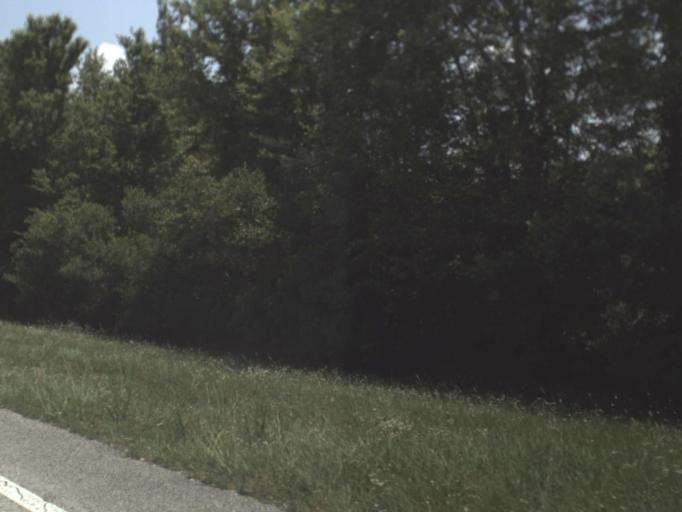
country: US
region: Florida
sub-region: Duval County
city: Baldwin
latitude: 30.2135
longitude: -82.0100
